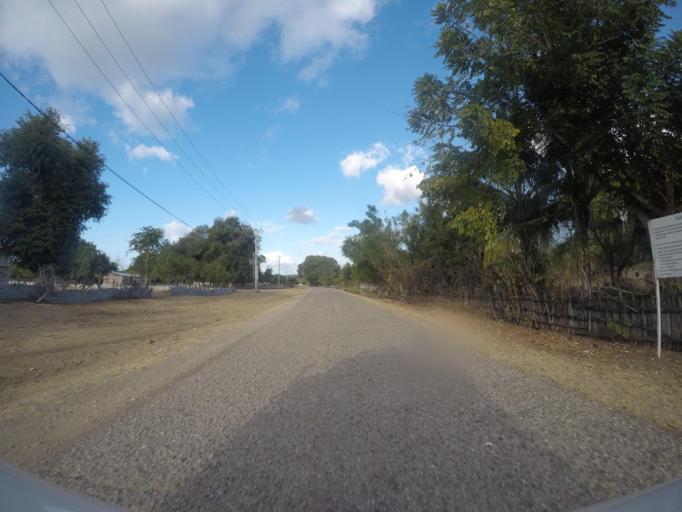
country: TL
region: Lautem
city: Lospalos
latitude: -8.3295
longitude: 126.9736
